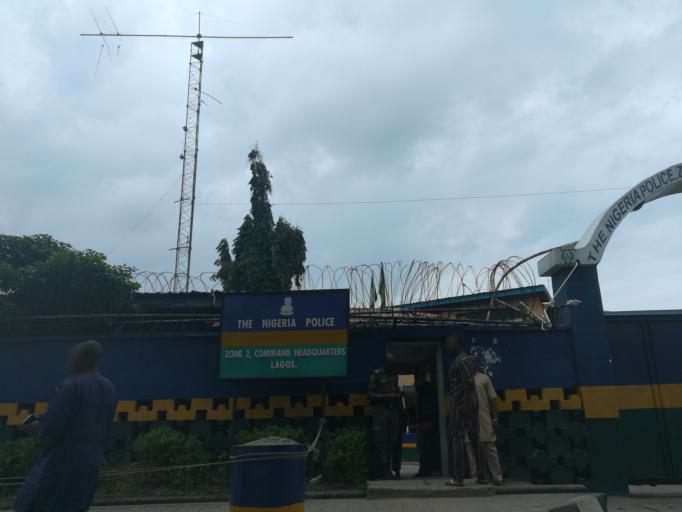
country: NG
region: Lagos
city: Lagos
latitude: 6.4423
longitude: 3.4028
